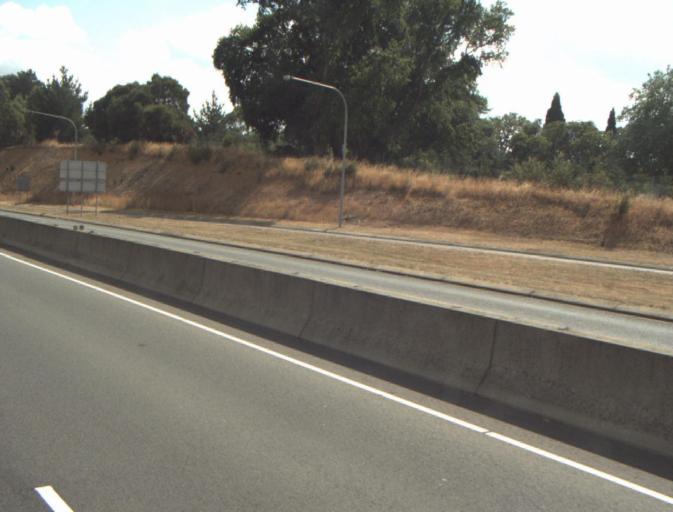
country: AU
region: Tasmania
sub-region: Launceston
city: Summerhill
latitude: -41.4701
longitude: 147.1428
